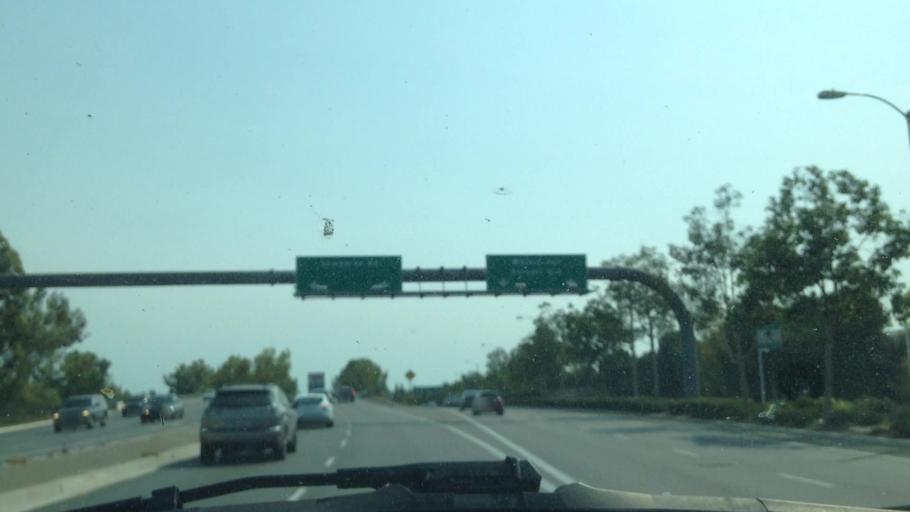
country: US
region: California
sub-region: Orange County
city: Tustin
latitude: 33.7176
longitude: -117.7976
